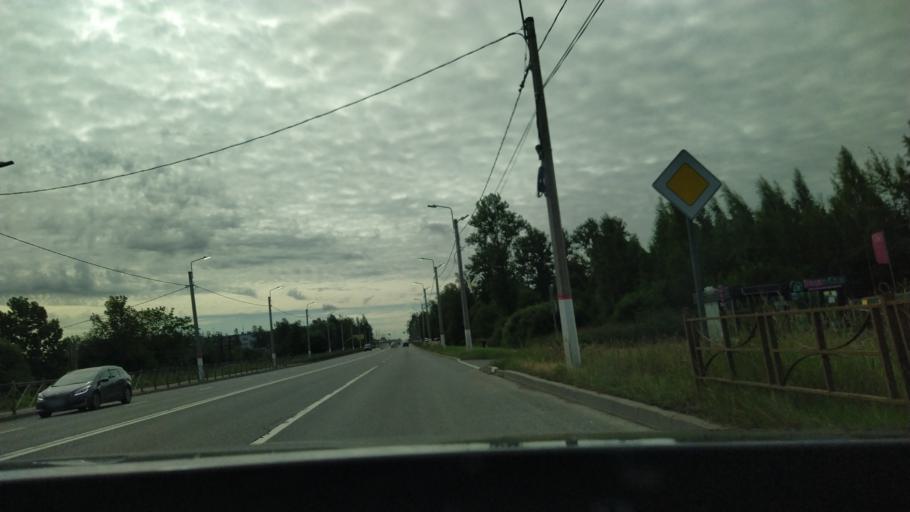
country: RU
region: Leningrad
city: Tosno
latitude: 59.5614
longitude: 30.8396
